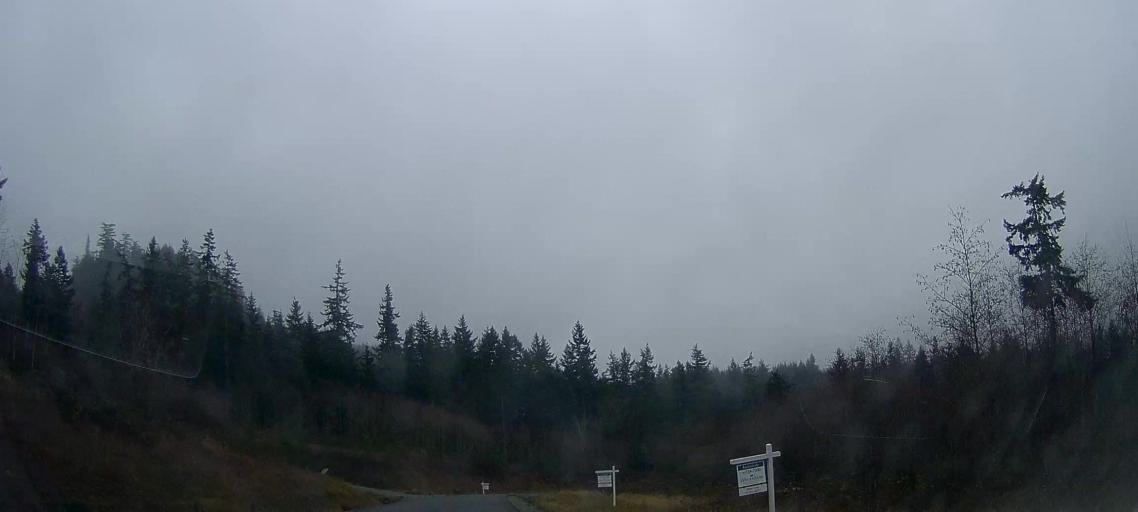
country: US
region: Washington
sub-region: Skagit County
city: Mount Vernon
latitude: 48.3679
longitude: -122.3011
